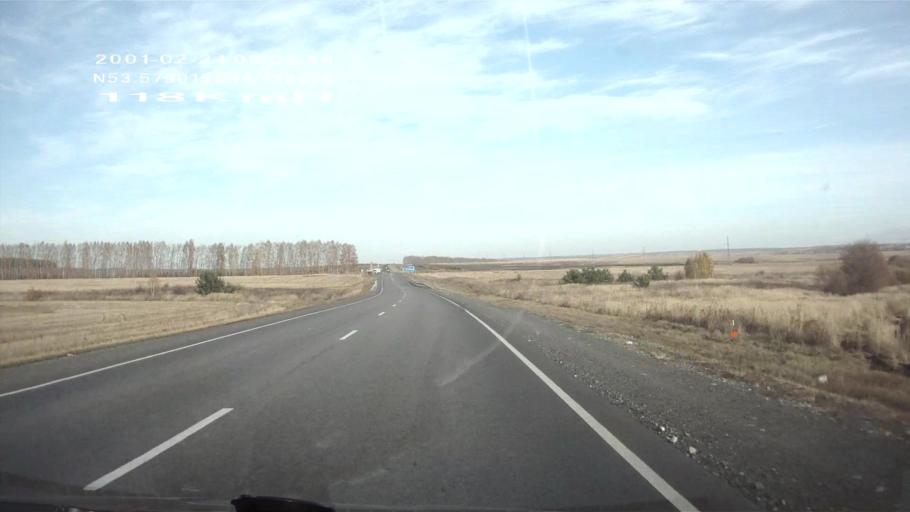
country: RU
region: Penza
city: Mokshan
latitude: 53.5790
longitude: 44.7286
